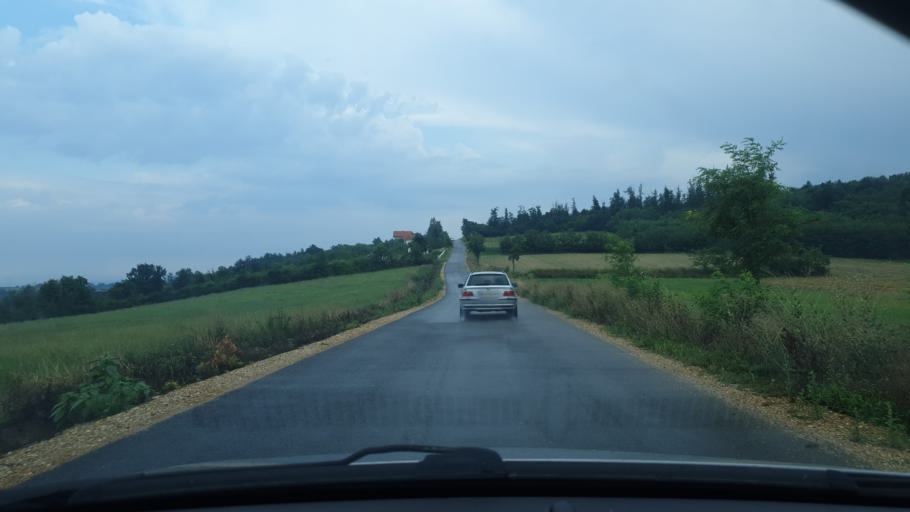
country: RS
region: Central Serbia
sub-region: Sumadijski Okrug
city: Kragujevac
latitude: 44.0628
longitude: 20.7847
